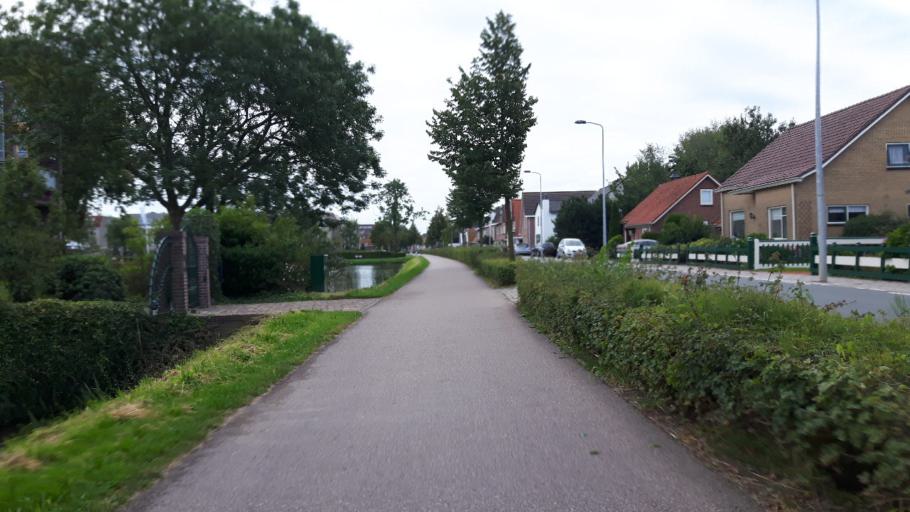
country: NL
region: North Holland
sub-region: Gemeente Hoorn
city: Hoorn
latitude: 52.6528
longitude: 5.0450
